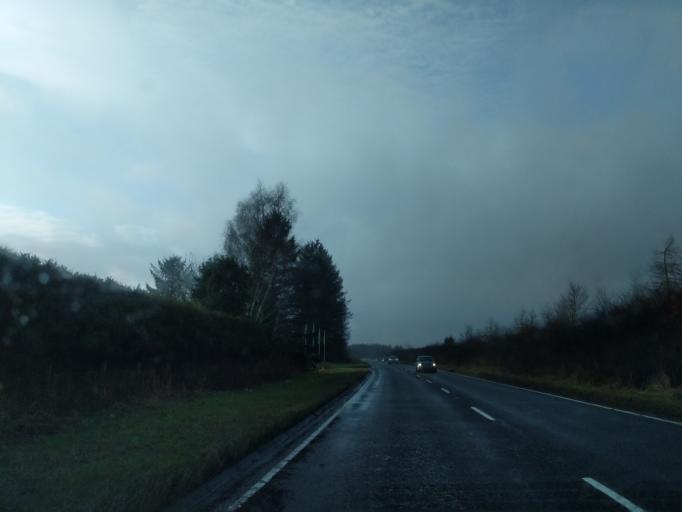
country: GB
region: Scotland
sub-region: Perth and Kinross
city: Kinross
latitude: 56.2075
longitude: -3.4620
